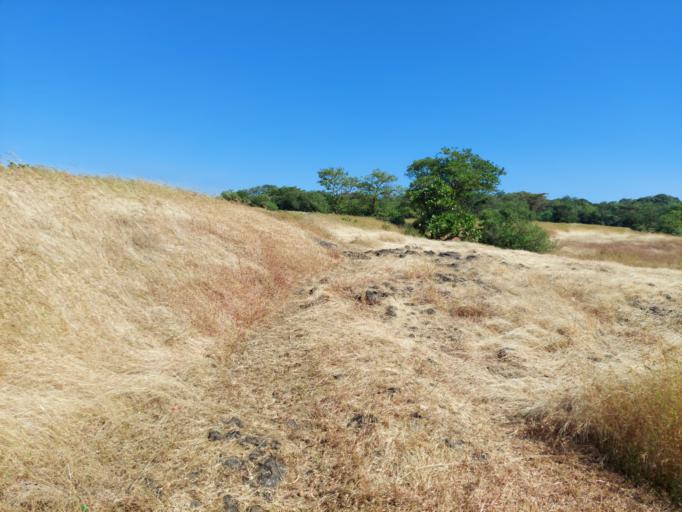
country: IN
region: Maharashtra
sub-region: Sindhudurg
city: Kudal
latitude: 16.0812
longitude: 73.8432
